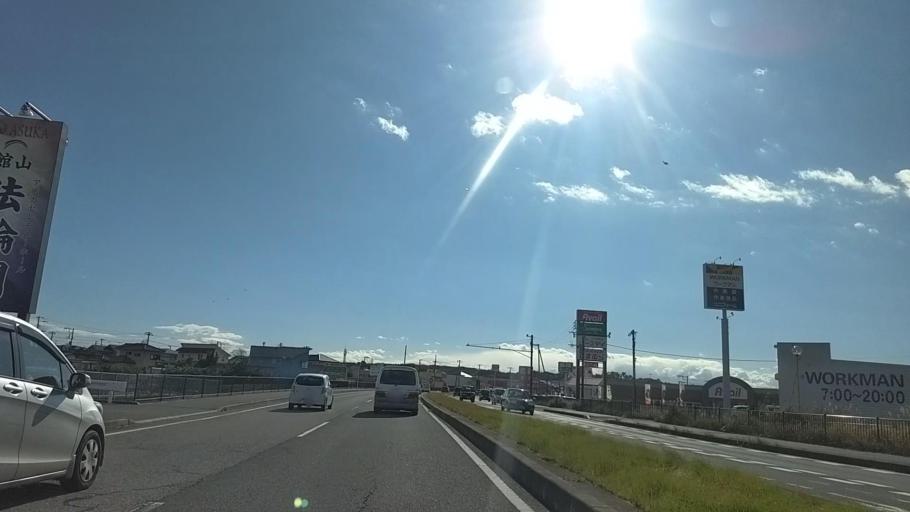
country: JP
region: Chiba
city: Tateyama
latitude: 34.9991
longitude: 139.8733
